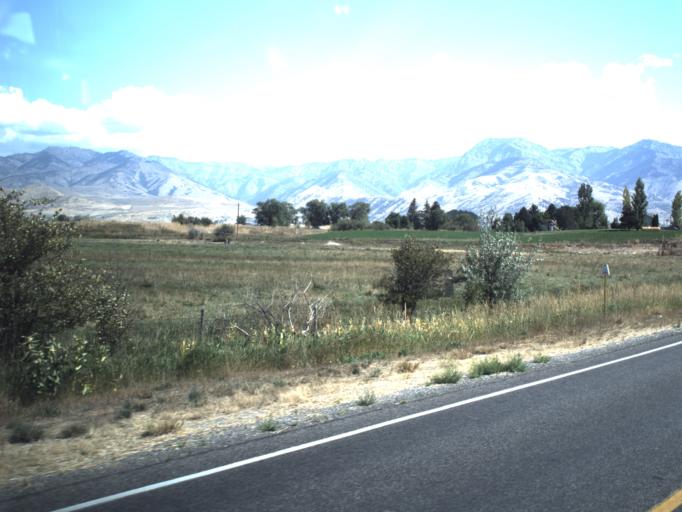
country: US
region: Utah
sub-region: Cache County
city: Smithfield
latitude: 41.8396
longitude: -111.8777
